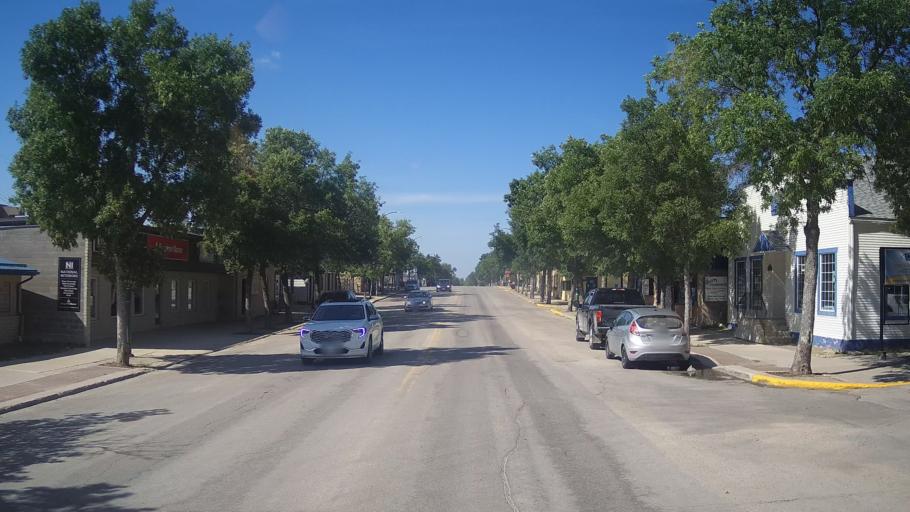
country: CA
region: Manitoba
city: Stonewall
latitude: 50.1335
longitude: -97.3266
